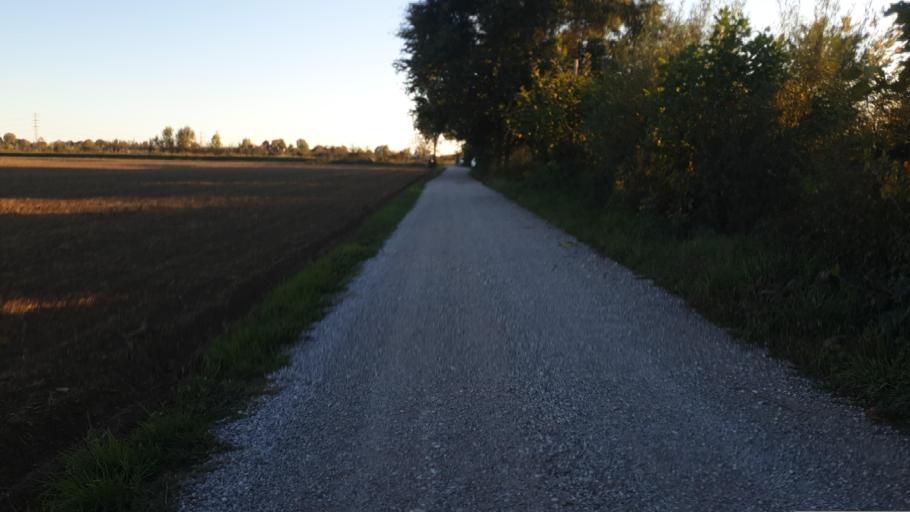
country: IT
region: Veneto
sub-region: Provincia di Venezia
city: Marano
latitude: 45.4471
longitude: 12.1002
